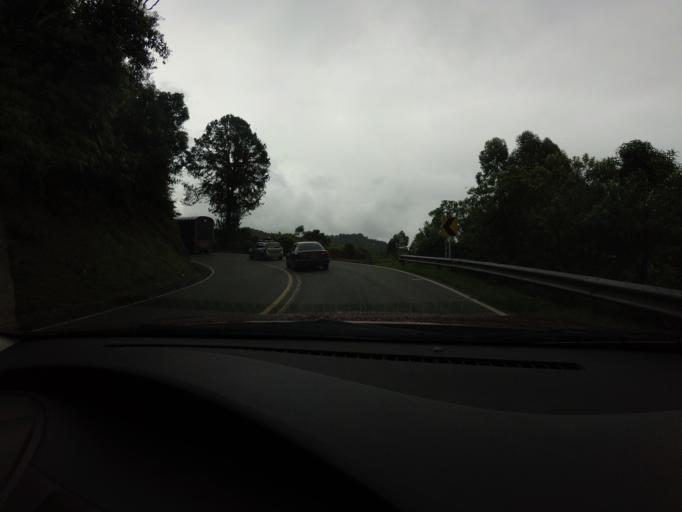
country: CO
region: Tolima
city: Herveo
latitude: 5.1419
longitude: -75.1593
